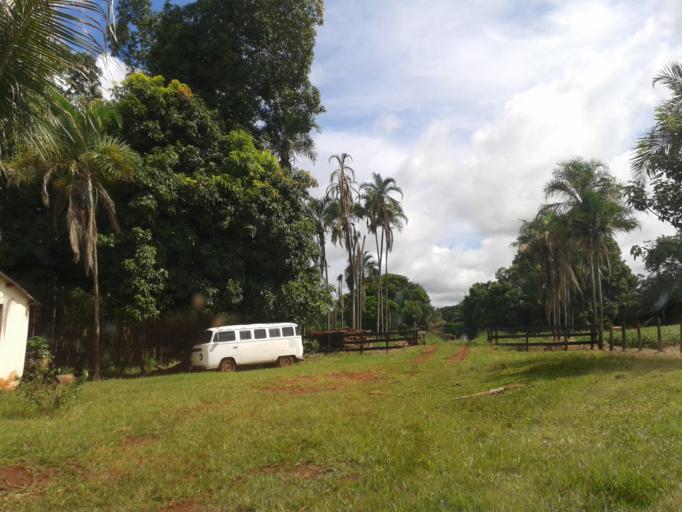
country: BR
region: Minas Gerais
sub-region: Santa Vitoria
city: Santa Vitoria
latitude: -18.7688
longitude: -49.8555
